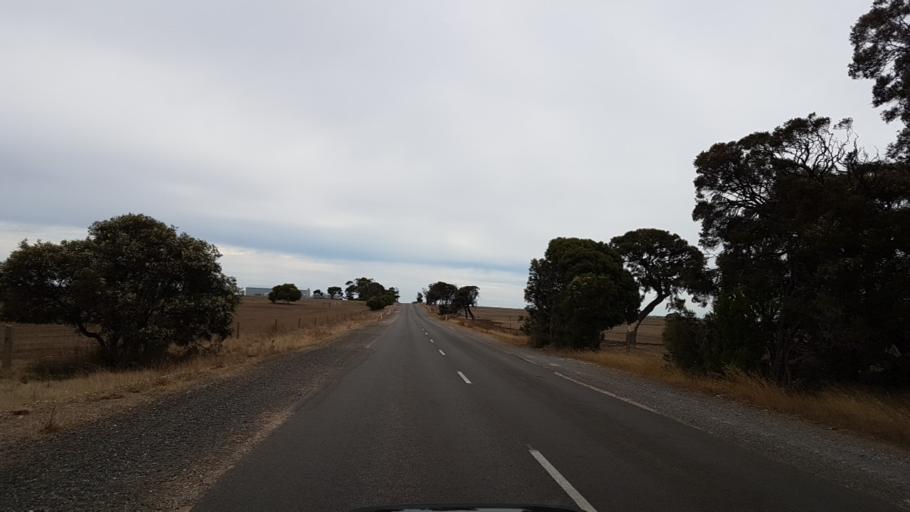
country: AU
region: South Australia
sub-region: Yorke Peninsula
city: Honiton
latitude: -34.9850
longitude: 137.2861
